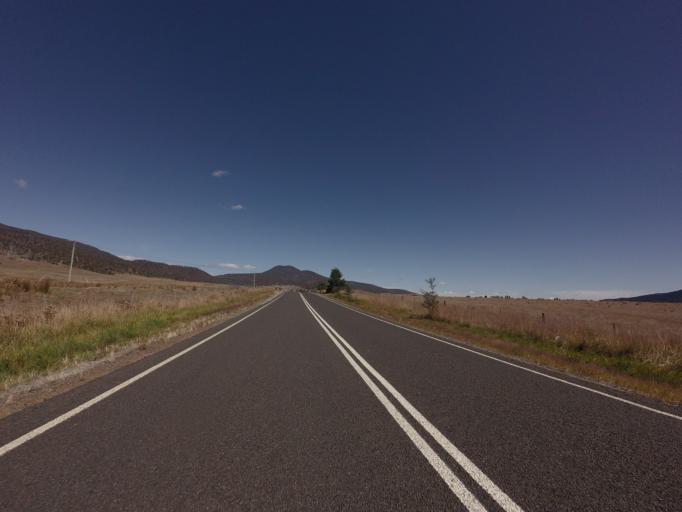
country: AU
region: Tasmania
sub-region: Break O'Day
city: St Helens
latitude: -41.7046
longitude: 147.8494
